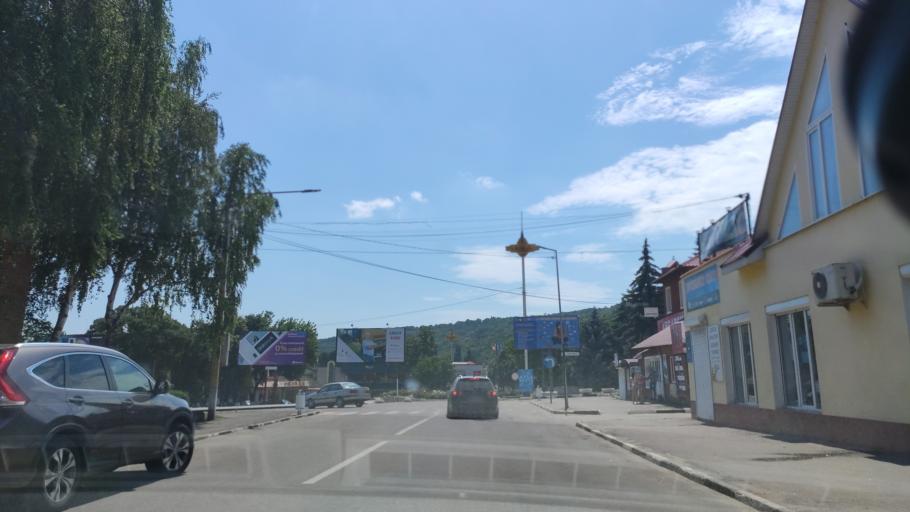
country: MD
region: Raionul Soroca
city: Soroca
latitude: 48.1579
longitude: 28.2996
